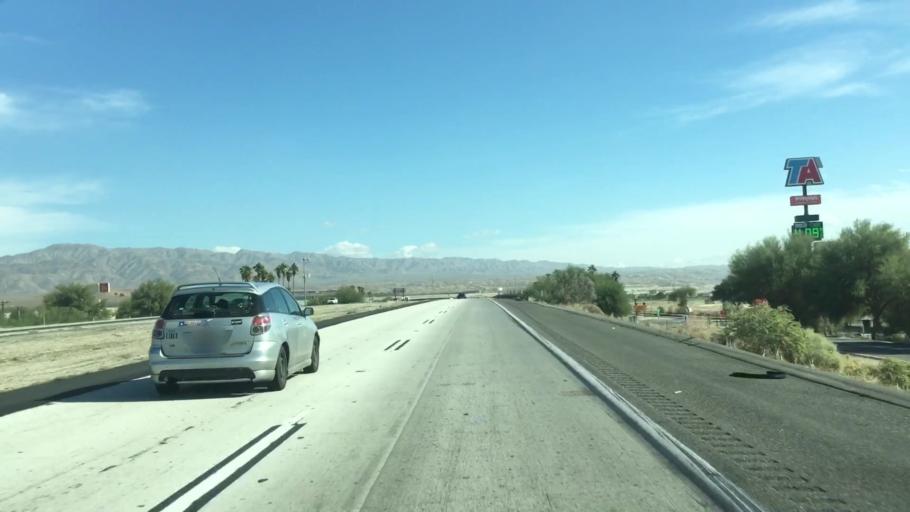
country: US
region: California
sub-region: Riverside County
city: Coachella
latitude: 33.7150
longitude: -116.1756
